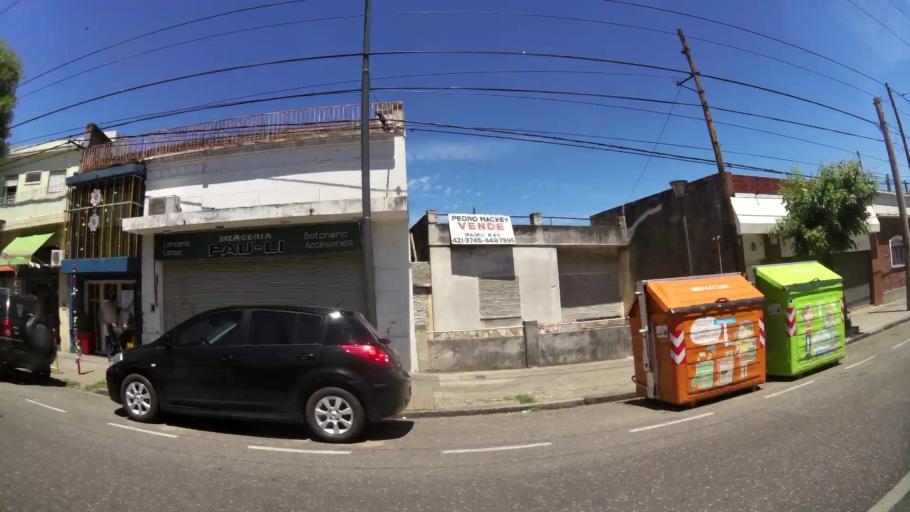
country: AR
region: Santa Fe
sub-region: Departamento de Rosario
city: Rosario
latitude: -32.9410
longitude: -60.6984
